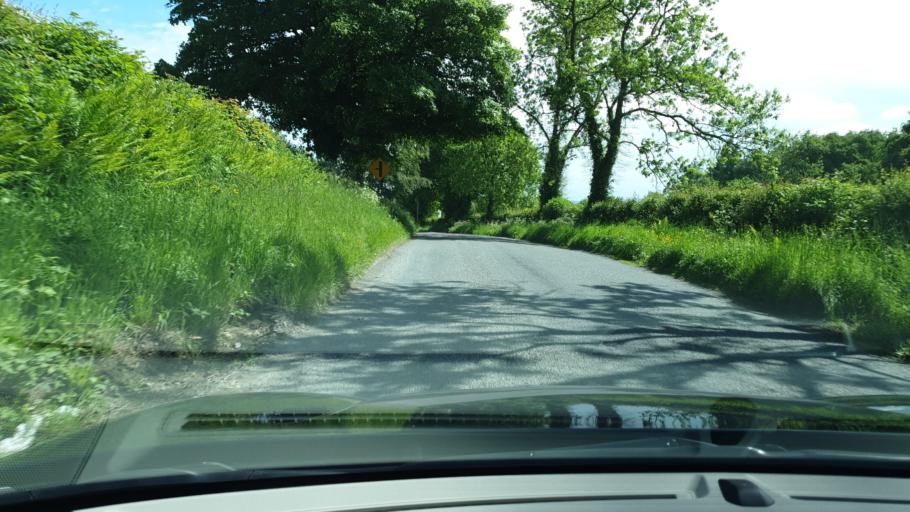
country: IE
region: Leinster
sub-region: An Mhi
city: Slane
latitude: 53.7492
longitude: -6.6014
